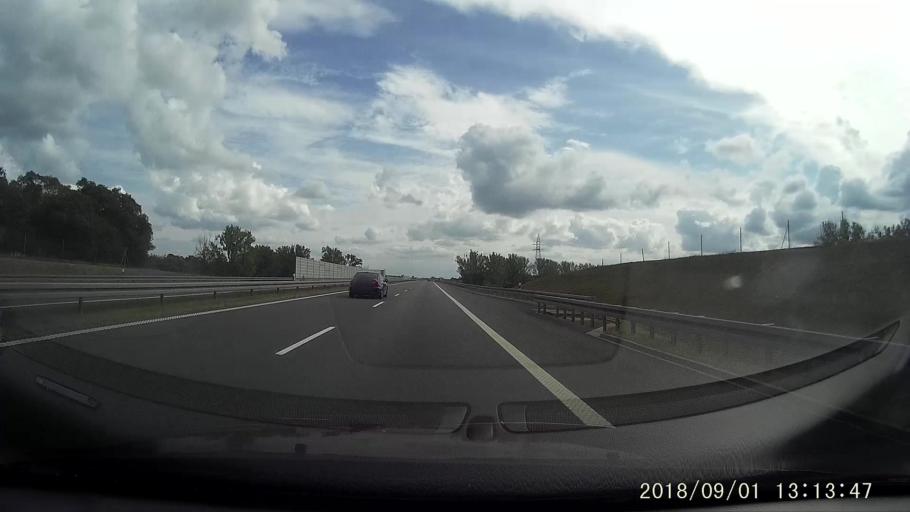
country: PL
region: West Pomeranian Voivodeship
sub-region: Powiat gryfinski
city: Gryfino
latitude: 53.2853
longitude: 14.6075
